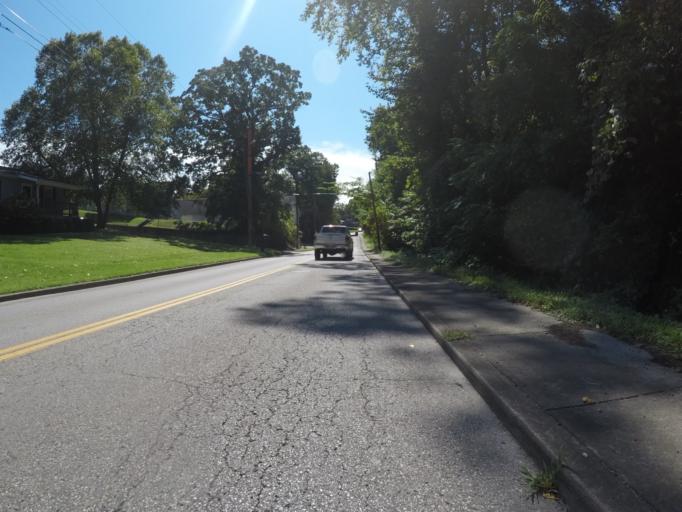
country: US
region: Kentucky
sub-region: Boyd County
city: Ashland
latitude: 38.4598
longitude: -82.6500
